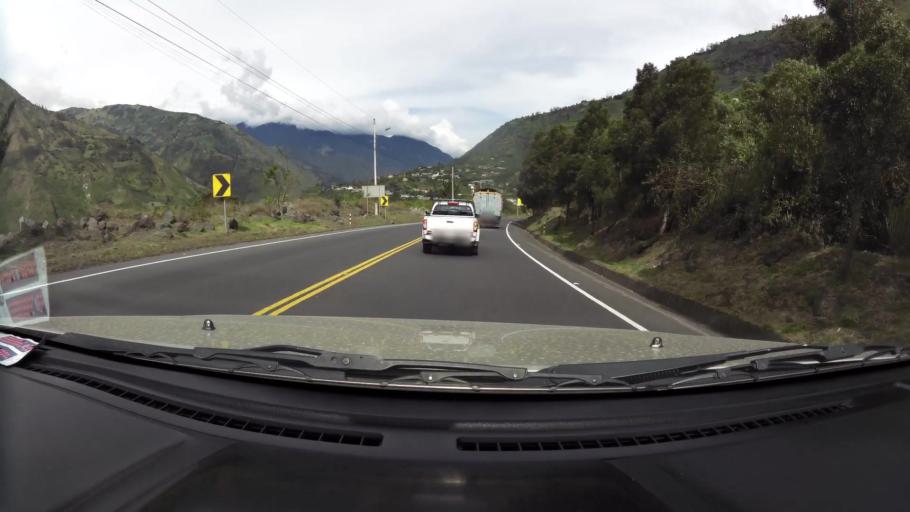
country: EC
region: Tungurahua
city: Banos
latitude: -1.4056
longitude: -78.4612
